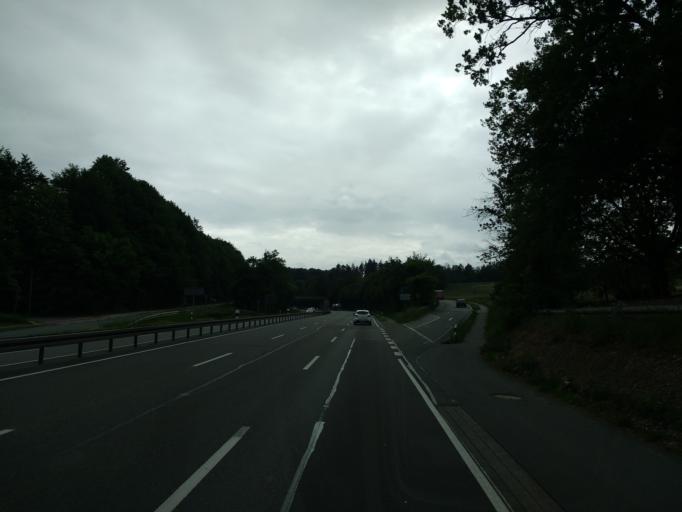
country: DE
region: Lower Saxony
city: Osnabrueck
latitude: 52.2402
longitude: 8.0603
